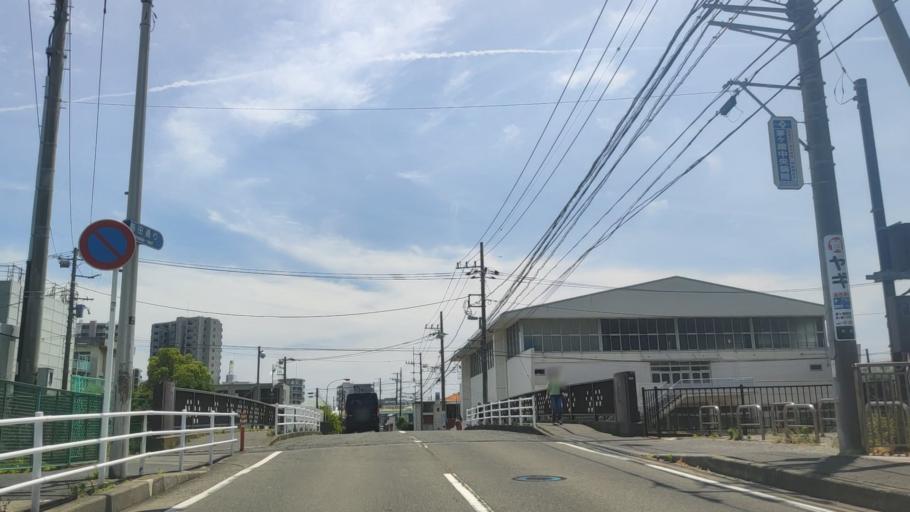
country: JP
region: Kanagawa
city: Chigasaki
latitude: 35.3337
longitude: 139.3996
